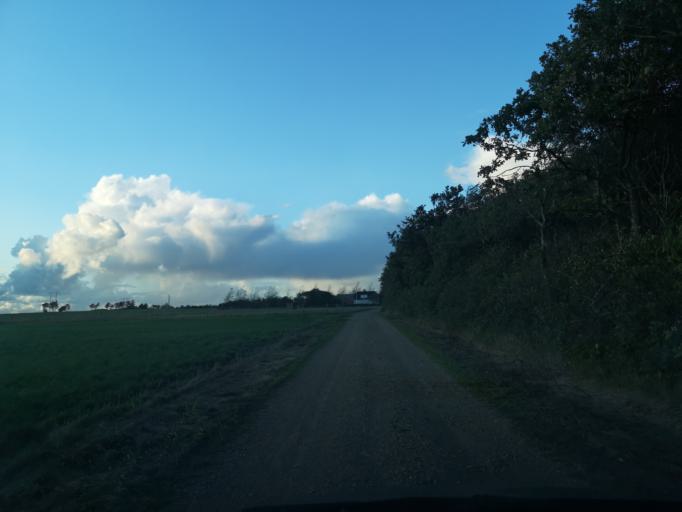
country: DK
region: Central Jutland
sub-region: Ringkobing-Skjern Kommune
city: Videbaek
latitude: 56.0464
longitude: 8.5881
